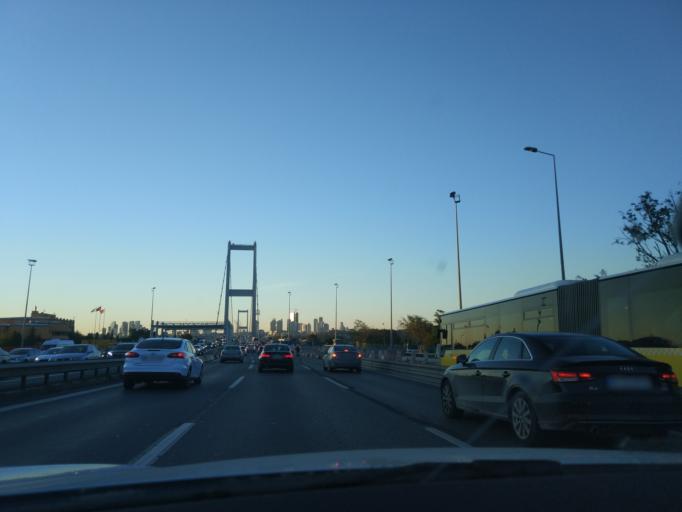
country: TR
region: Istanbul
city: UEskuedar
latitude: 41.0378
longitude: 29.0425
